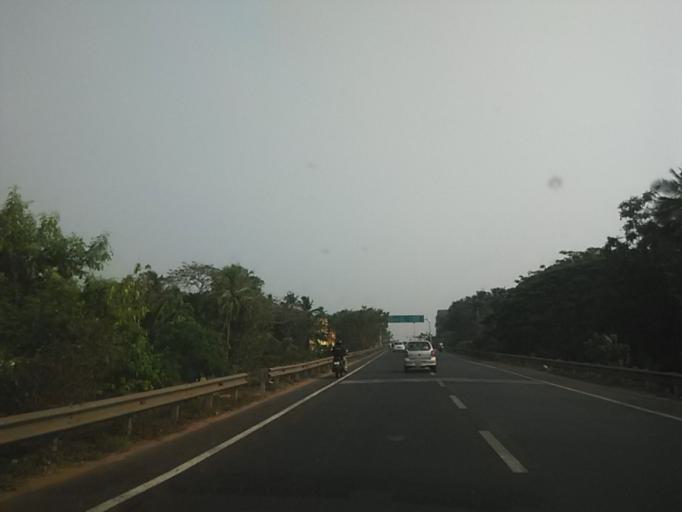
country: IN
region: Kerala
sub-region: Kozhikode
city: Kozhikode
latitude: 11.2912
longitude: 75.7990
